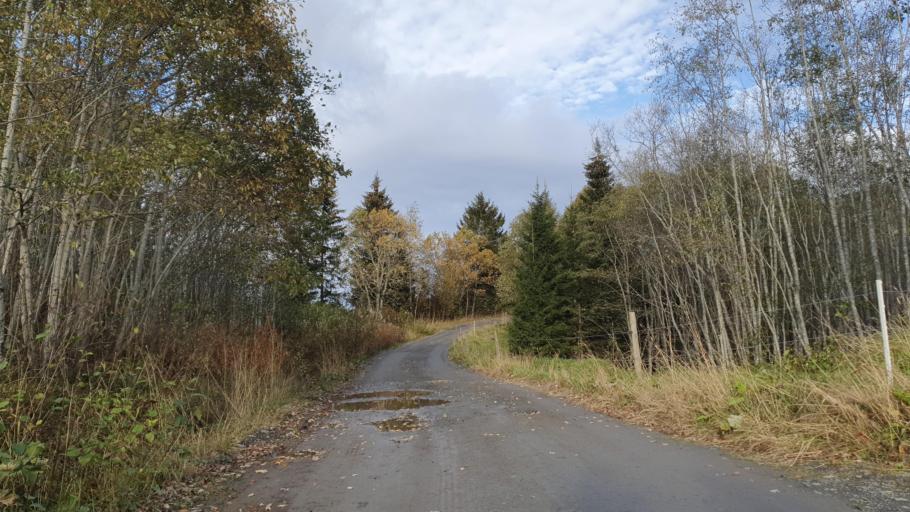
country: NO
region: Sor-Trondelag
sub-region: Klaebu
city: Klaebu
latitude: 63.2894
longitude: 10.4612
